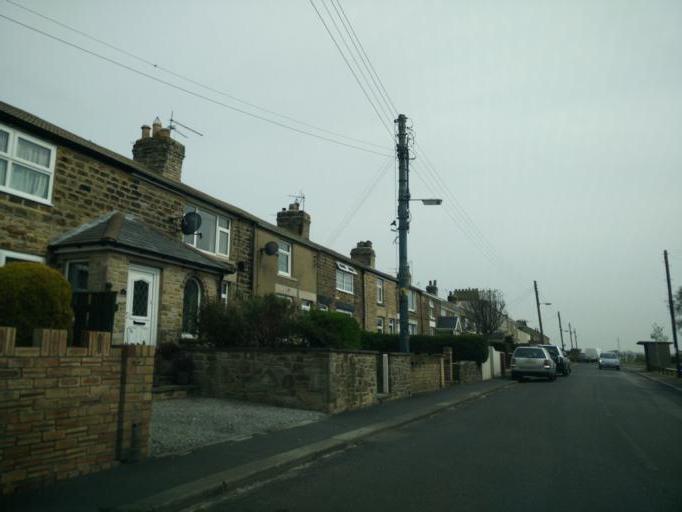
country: GB
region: England
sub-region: County Durham
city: Crook
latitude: 54.6899
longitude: -1.7333
